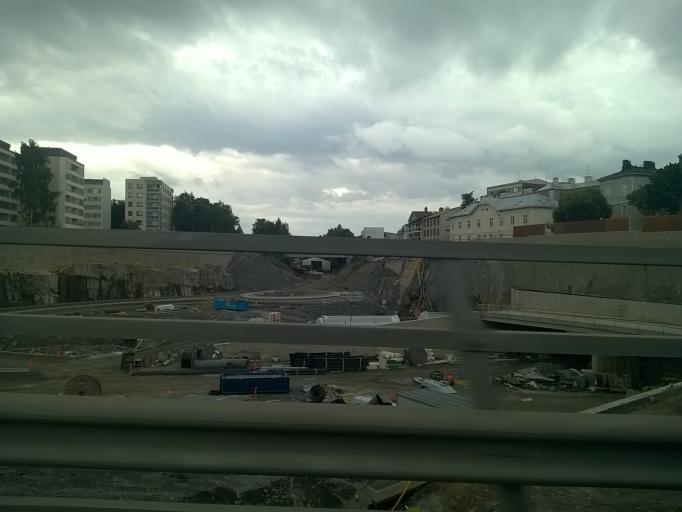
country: FI
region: Pirkanmaa
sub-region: Tampere
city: Tampere
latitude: 61.5078
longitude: 23.7738
